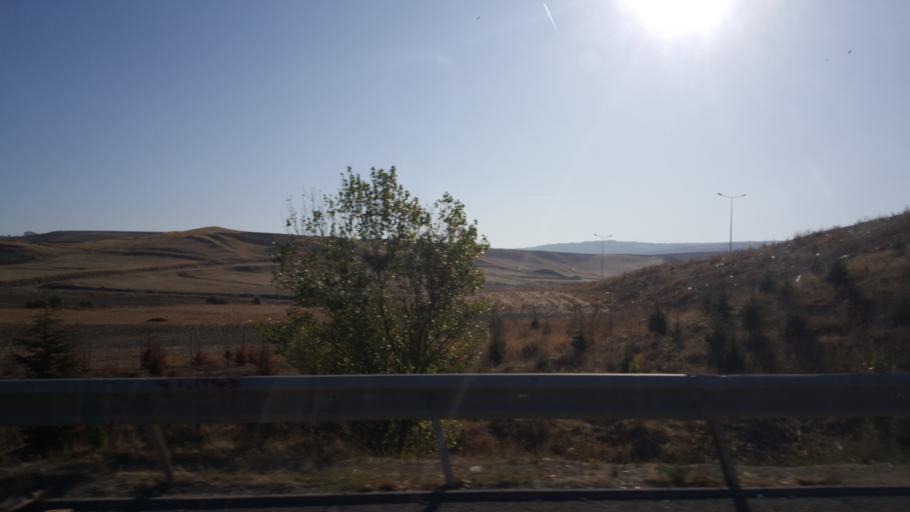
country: TR
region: Ankara
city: Mamak
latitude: 39.8804
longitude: 32.9511
